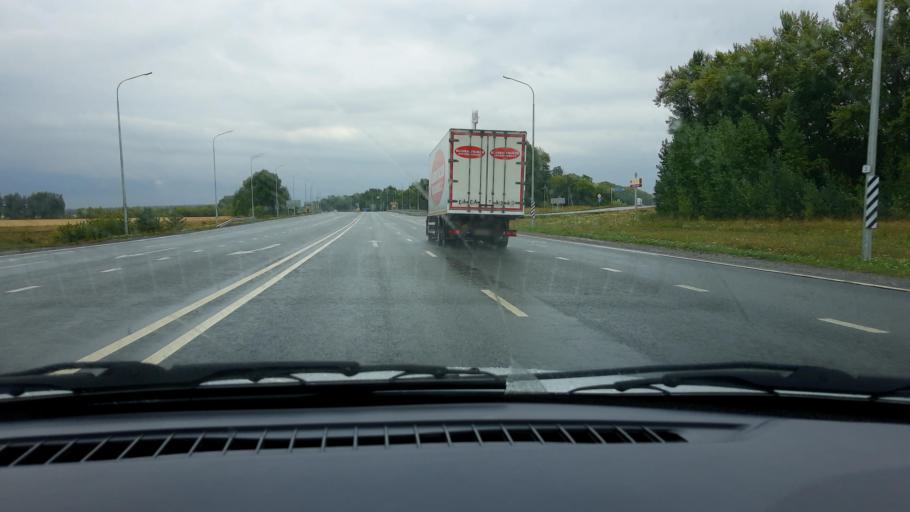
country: RU
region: Chuvashia
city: Yantikovo
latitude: 55.7888
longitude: 47.7304
